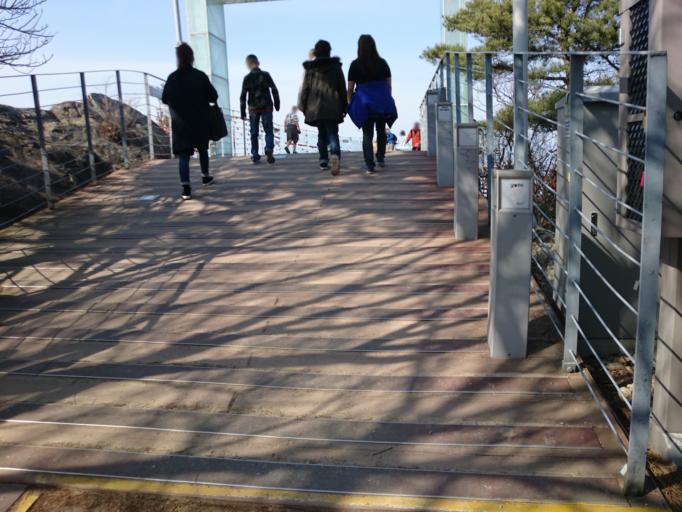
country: KR
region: Daegu
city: Daegu
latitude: 35.8246
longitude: 128.5795
